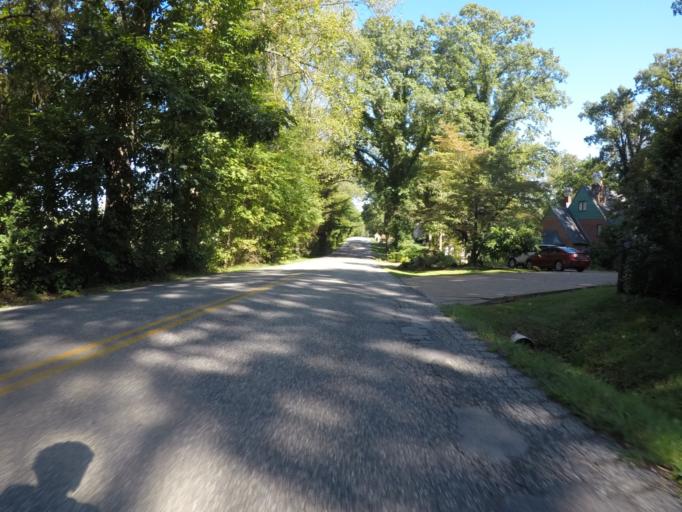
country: US
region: Kentucky
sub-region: Greenup County
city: Russell
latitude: 38.4939
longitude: -82.6948
